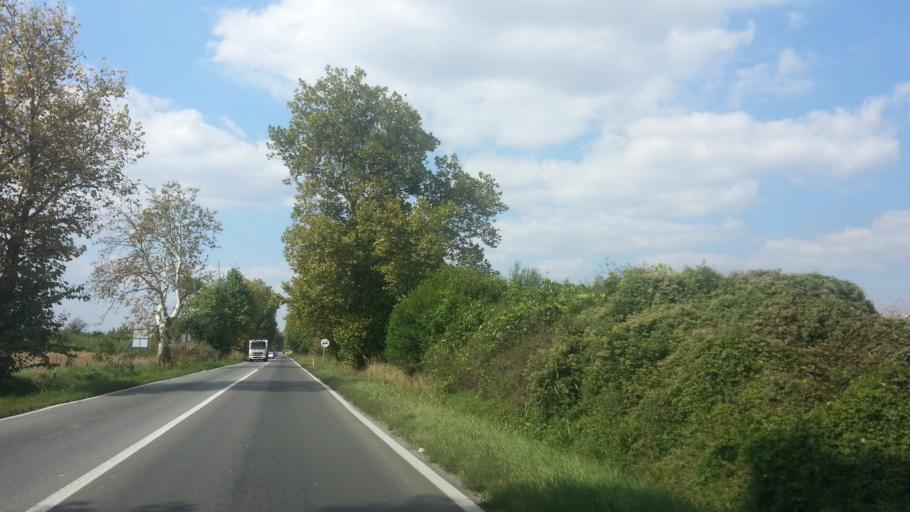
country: RS
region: Central Serbia
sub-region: Belgrade
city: Zemun
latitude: 44.8756
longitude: 20.3399
